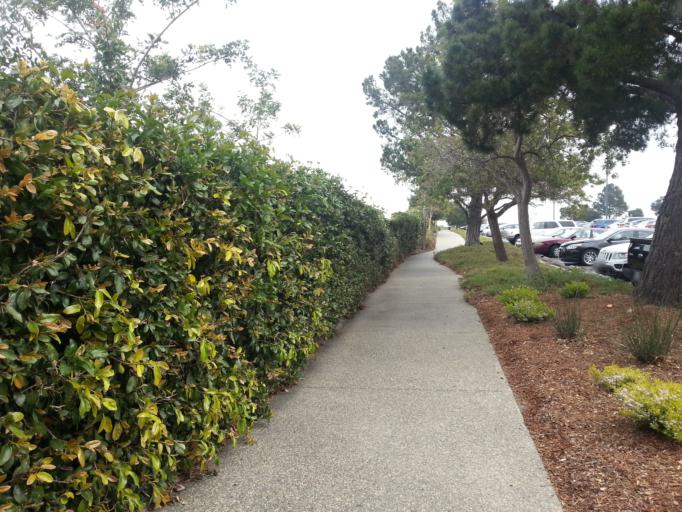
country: US
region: California
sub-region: San Mateo County
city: Burlingame
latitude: 37.5953
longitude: -122.3646
